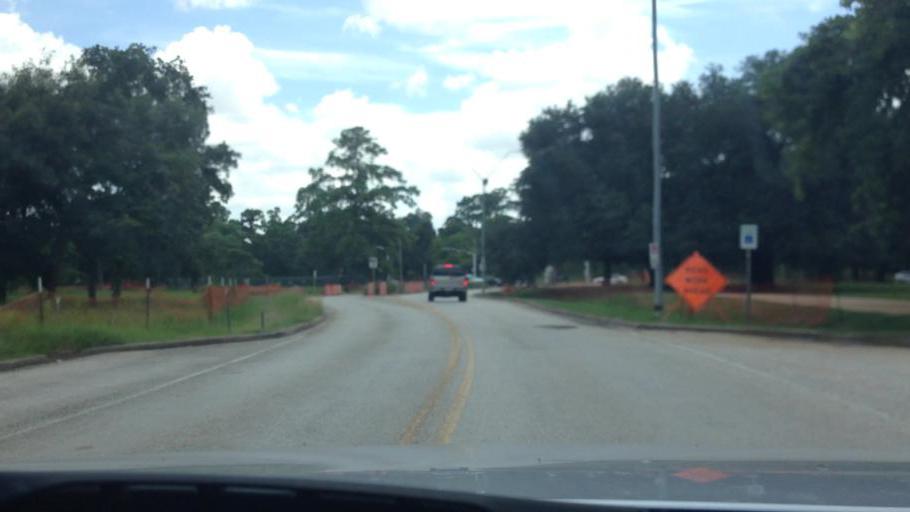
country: US
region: Texas
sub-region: Harris County
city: West University Place
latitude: 29.7657
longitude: -95.4308
